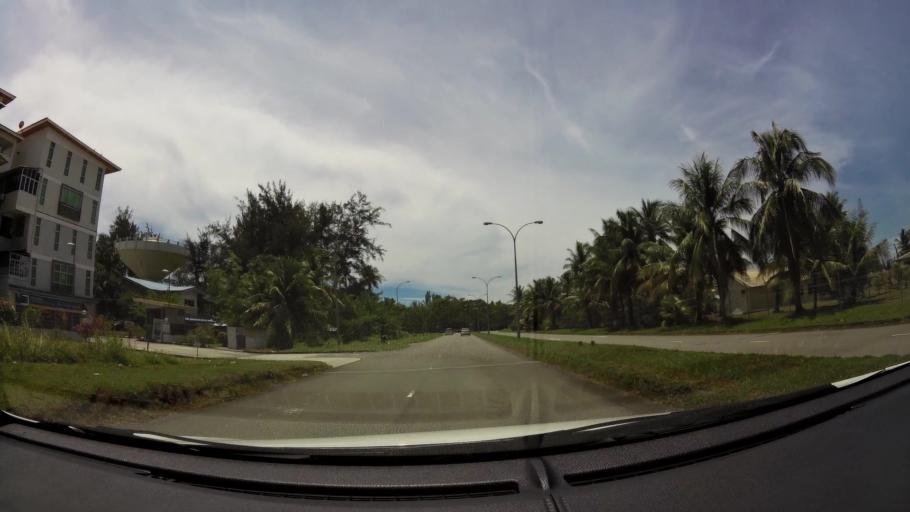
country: BN
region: Belait
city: Kuala Belait
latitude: 4.5913
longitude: 114.2307
